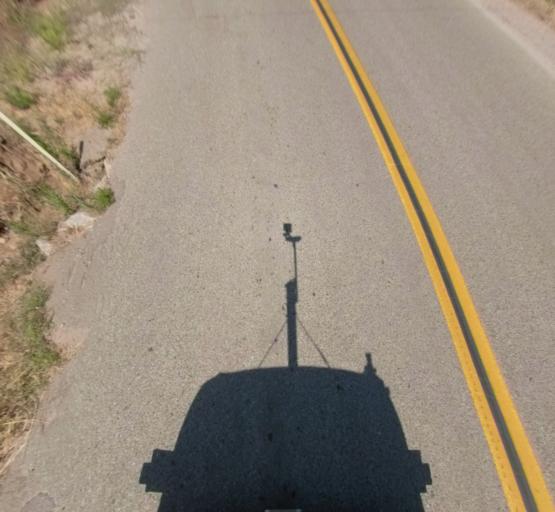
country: US
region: California
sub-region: Fresno County
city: Auberry
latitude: 37.2367
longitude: -119.4722
